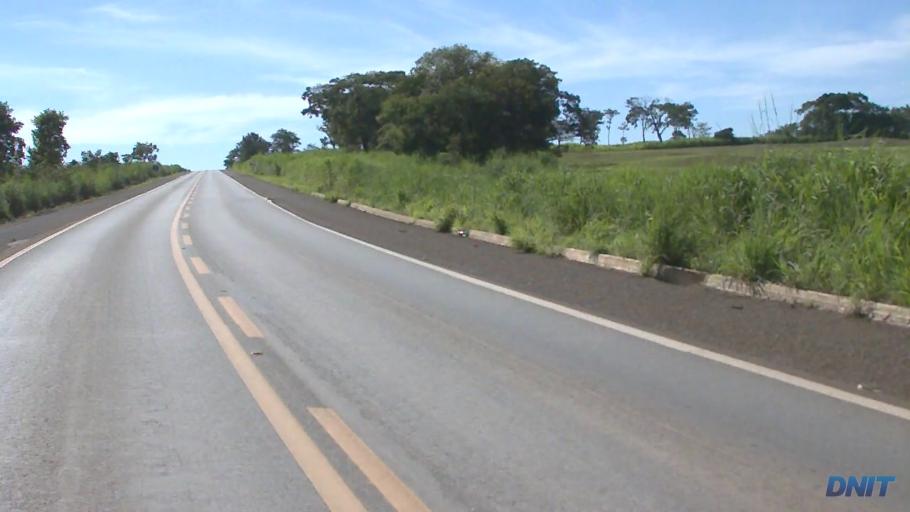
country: BR
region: Goias
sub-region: Padre Bernardo
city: Padre Bernardo
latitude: -15.2100
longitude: -48.4829
